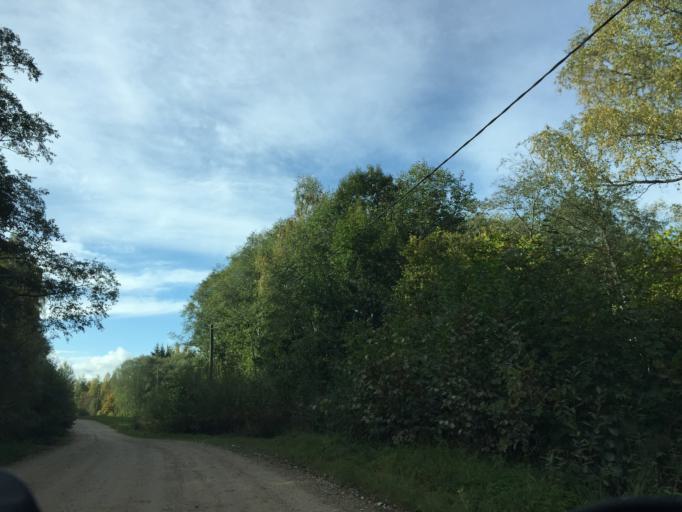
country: LV
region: Jaunpils
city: Jaunpils
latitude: 56.6100
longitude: 23.0045
